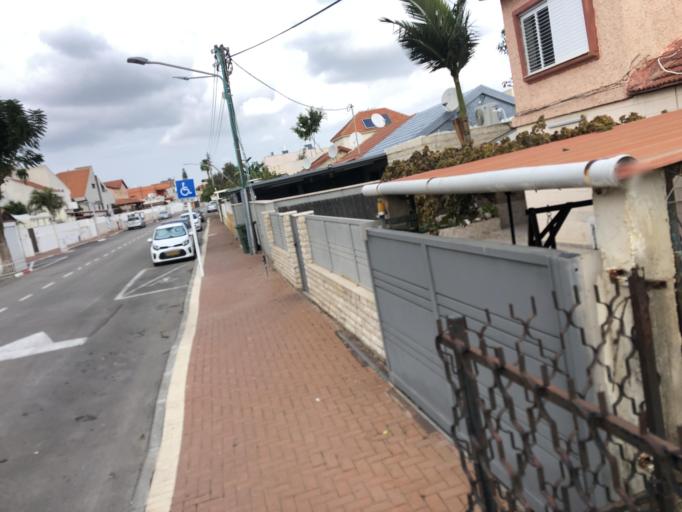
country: IL
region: Northern District
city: `Akko
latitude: 32.9330
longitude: 35.0950
